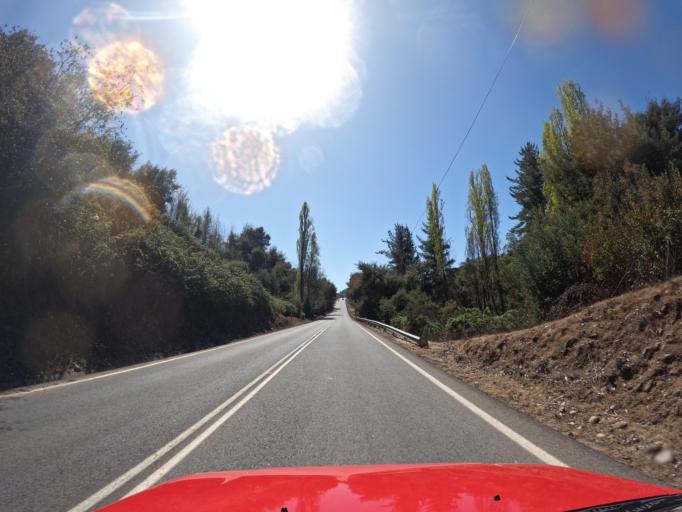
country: CL
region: Maule
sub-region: Provincia de Talca
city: San Clemente
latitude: -35.4548
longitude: -71.2691
